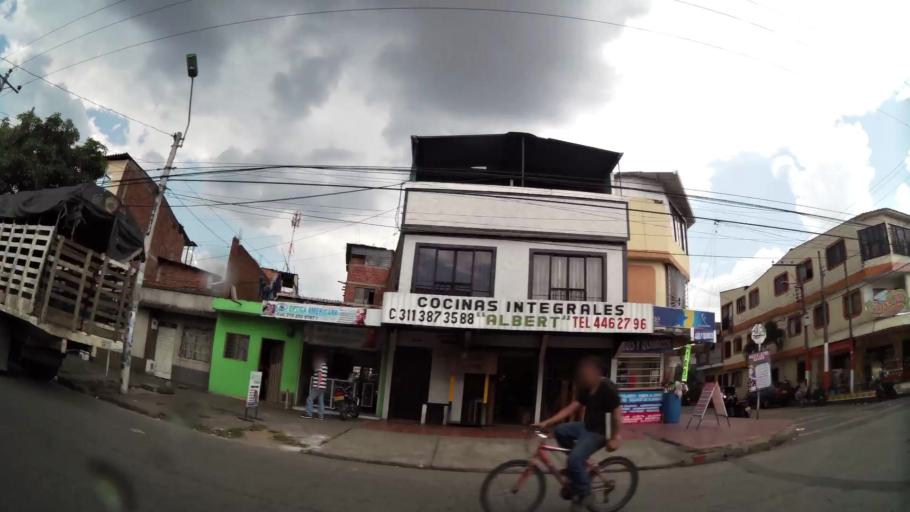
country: CO
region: Valle del Cauca
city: Cali
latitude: 3.4740
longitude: -76.5100
